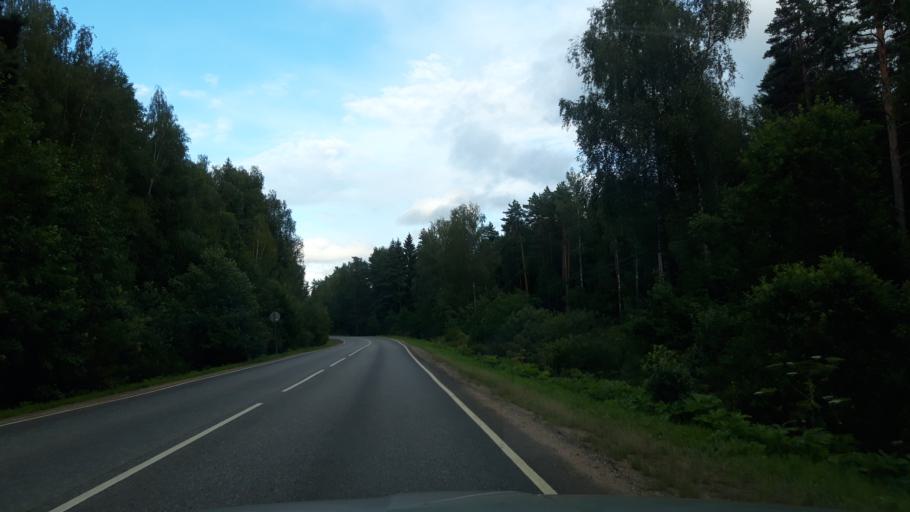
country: RU
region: Moskovskaya
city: Solnechnogorsk
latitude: 56.0936
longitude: 36.8951
